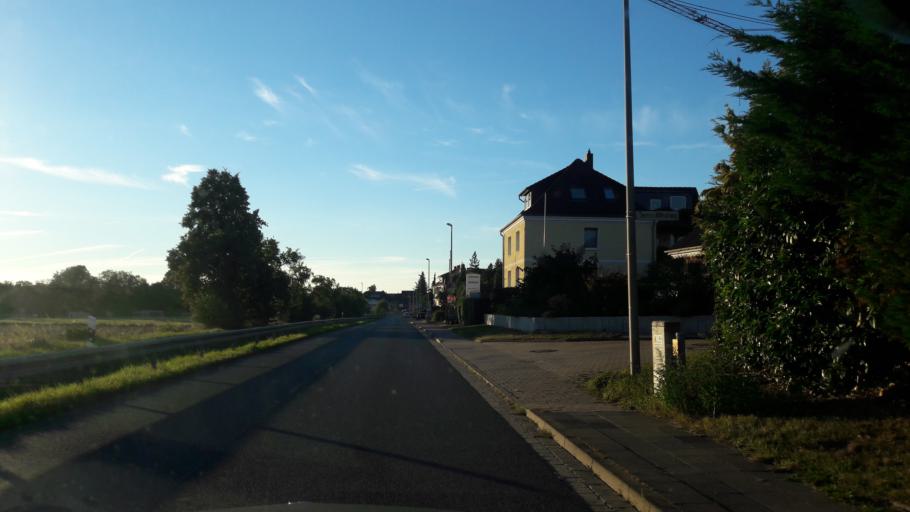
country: DE
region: Lower Saxony
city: Hildesheim
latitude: 52.1146
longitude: 9.9880
